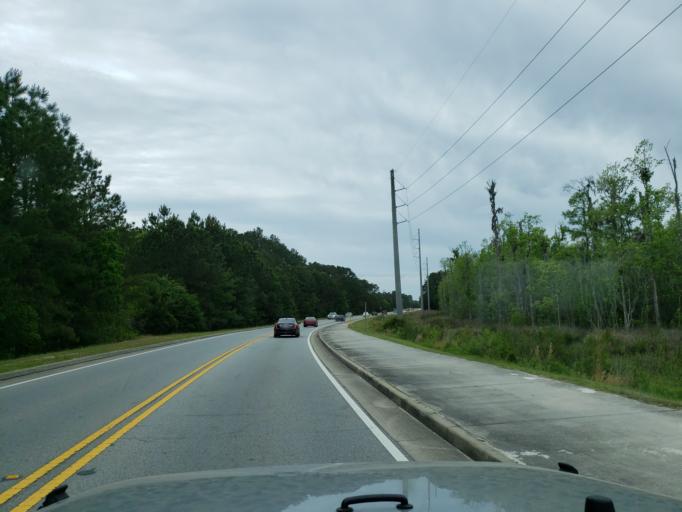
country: US
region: Georgia
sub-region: Chatham County
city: Pooler
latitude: 32.1595
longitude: -81.2335
